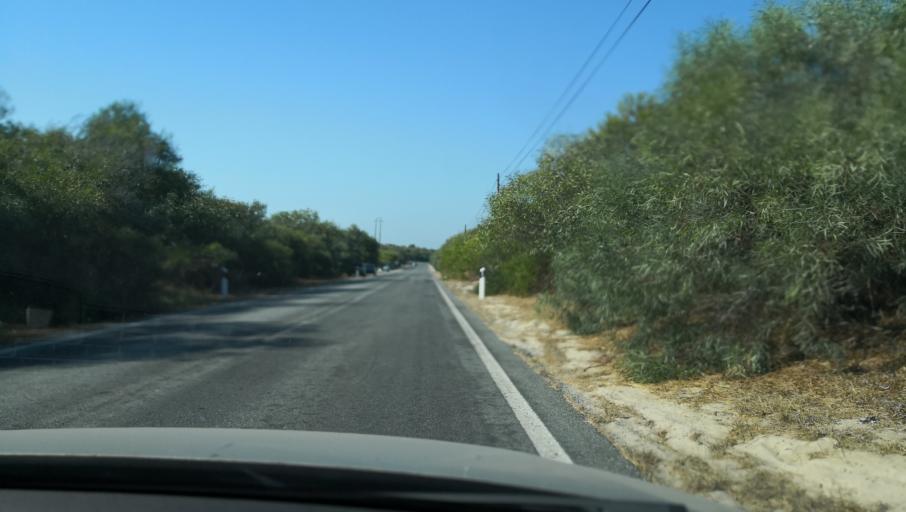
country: PT
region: Setubal
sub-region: Setubal
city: Setubal
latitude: 38.4093
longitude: -8.8120
